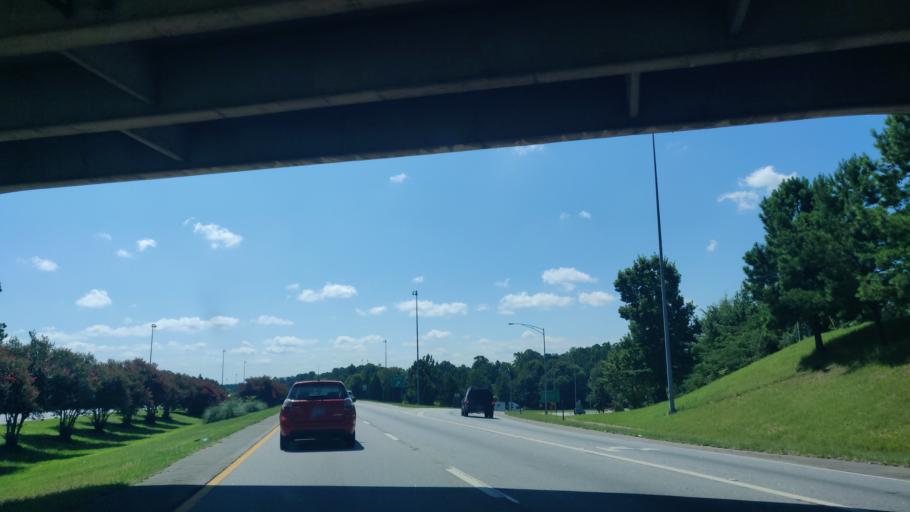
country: US
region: Alabama
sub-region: Russell County
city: Phenix City
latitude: 32.4568
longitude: -85.0125
